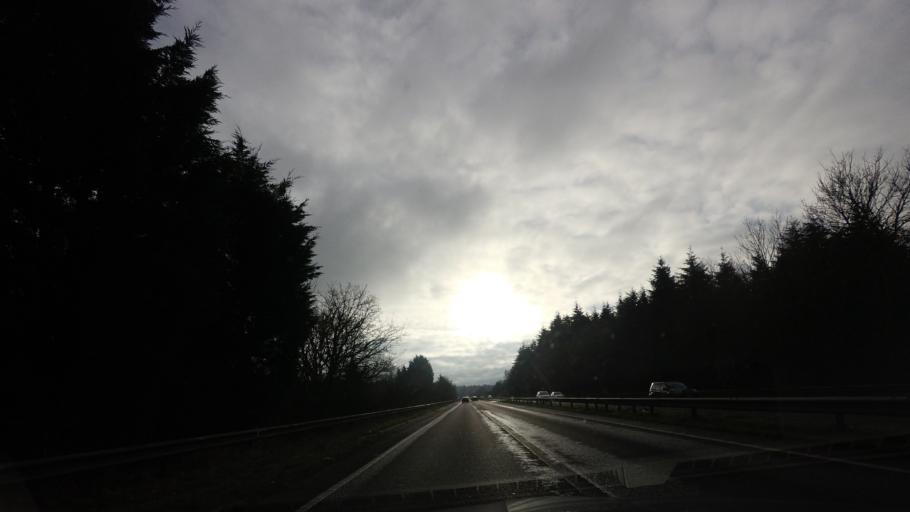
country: GB
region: England
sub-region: Kent
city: Sevenoaks
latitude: 51.2621
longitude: 0.1713
